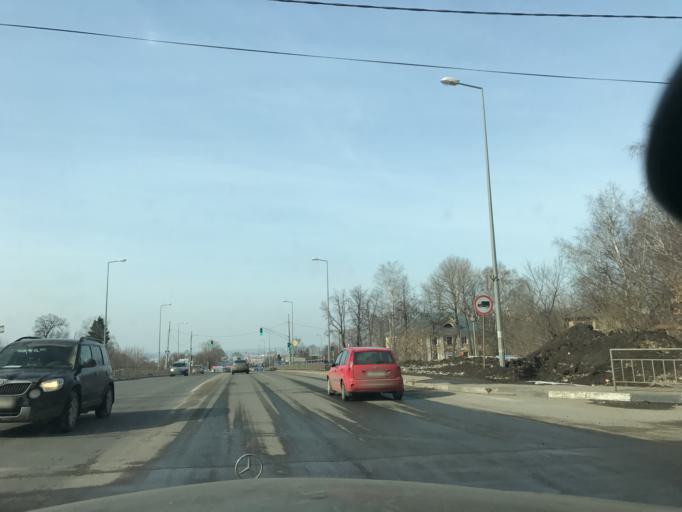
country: RU
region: Nizjnij Novgorod
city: Nizhniy Novgorod
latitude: 56.3109
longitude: 43.9811
